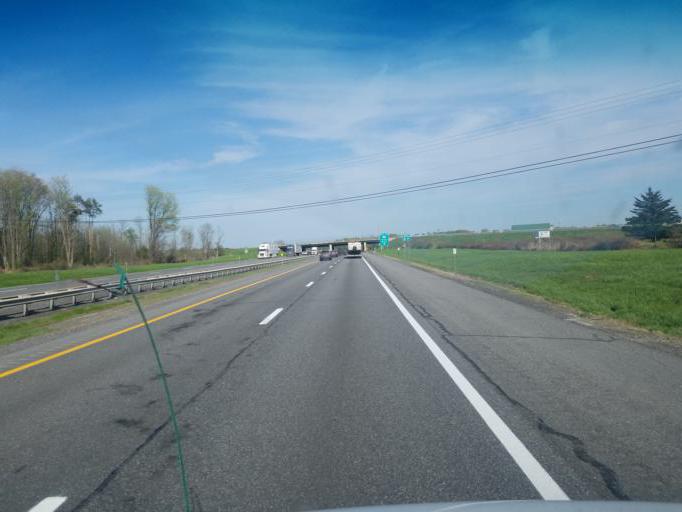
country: US
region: New York
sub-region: Oneida County
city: Sherrill
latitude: 43.1244
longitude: -75.5931
